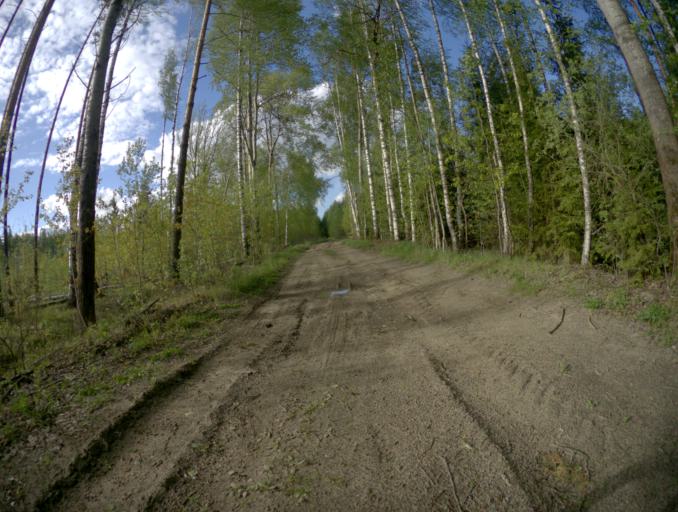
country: RU
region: Vladimir
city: Gusevskiy
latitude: 55.6066
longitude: 40.5415
